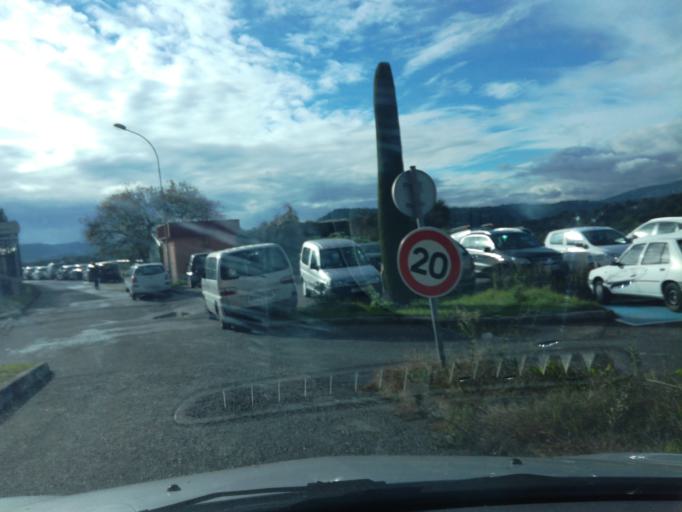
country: FR
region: Provence-Alpes-Cote d'Azur
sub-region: Departement des Alpes-Maritimes
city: Pegomas
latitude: 43.6208
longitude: 6.9300
